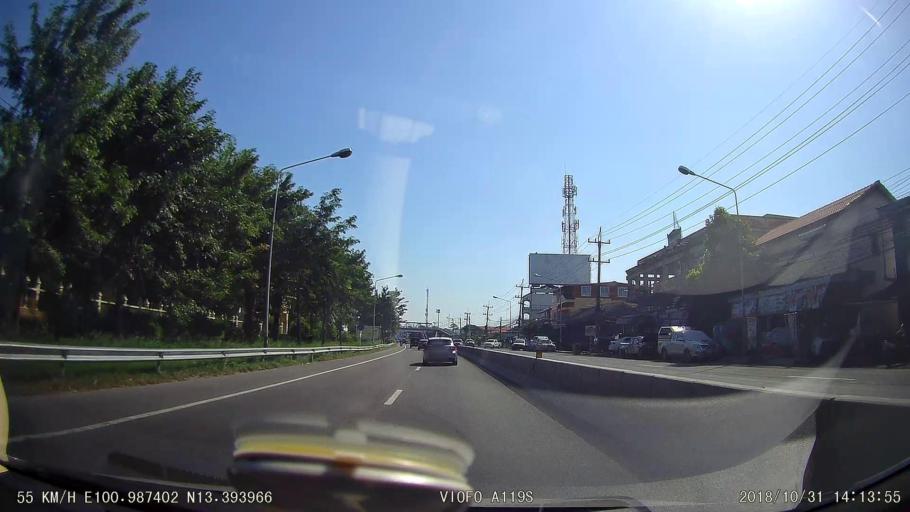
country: TH
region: Chon Buri
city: Chon Buri
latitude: 13.3938
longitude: 100.9874
